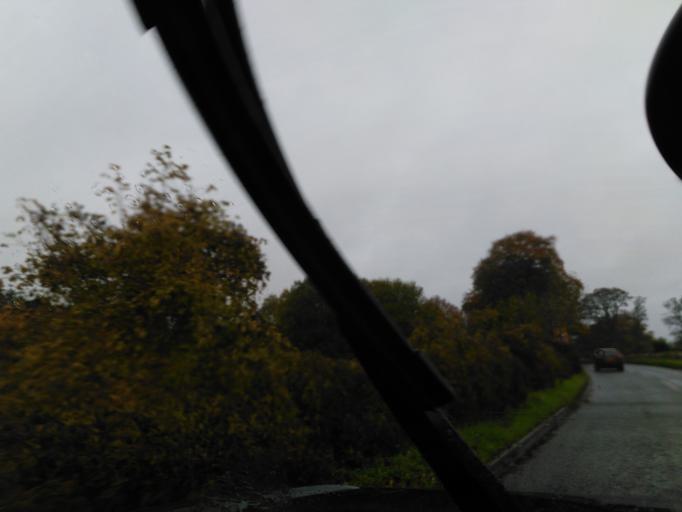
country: GB
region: England
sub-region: Bath and North East Somerset
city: Freshford
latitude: 51.3480
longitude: -2.2975
